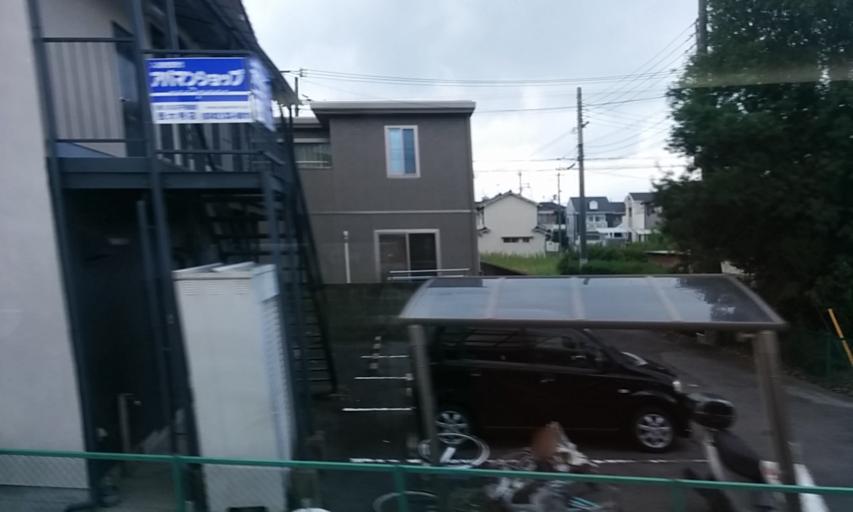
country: JP
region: Nara
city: Nara-shi
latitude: 34.6618
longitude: 135.7836
